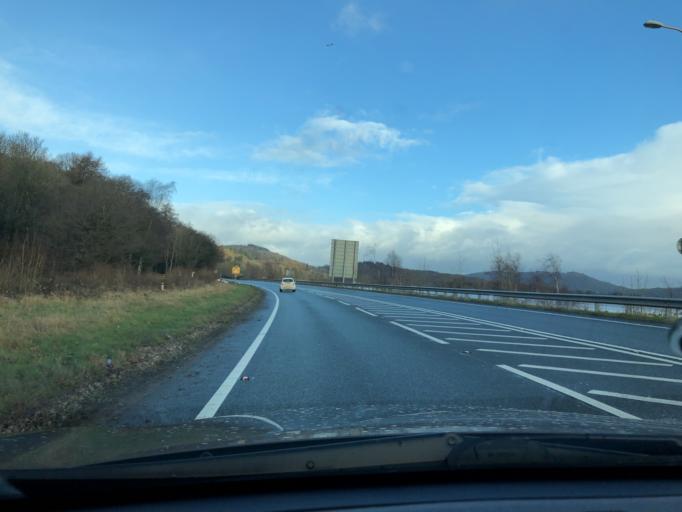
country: GB
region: England
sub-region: Cumbria
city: Ulverston
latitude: 54.2370
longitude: -3.0488
